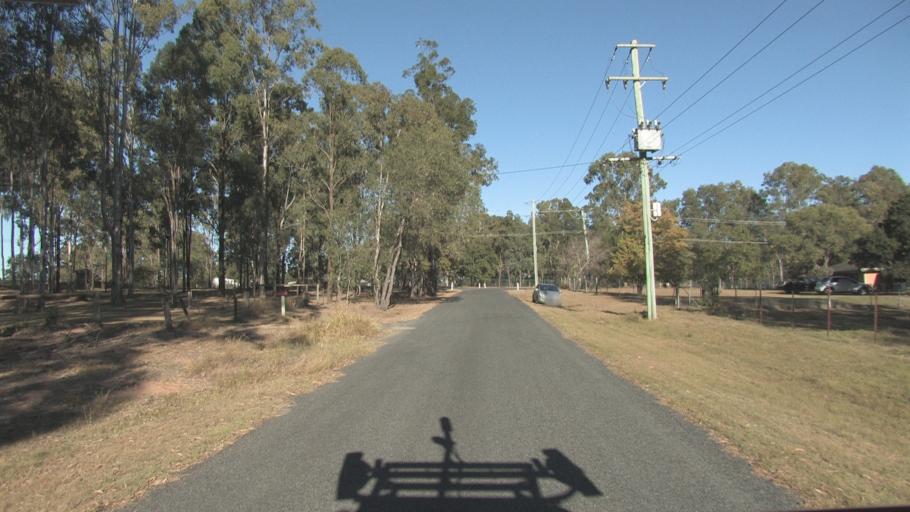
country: AU
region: Queensland
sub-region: Logan
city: North Maclean
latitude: -27.7969
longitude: 152.9936
